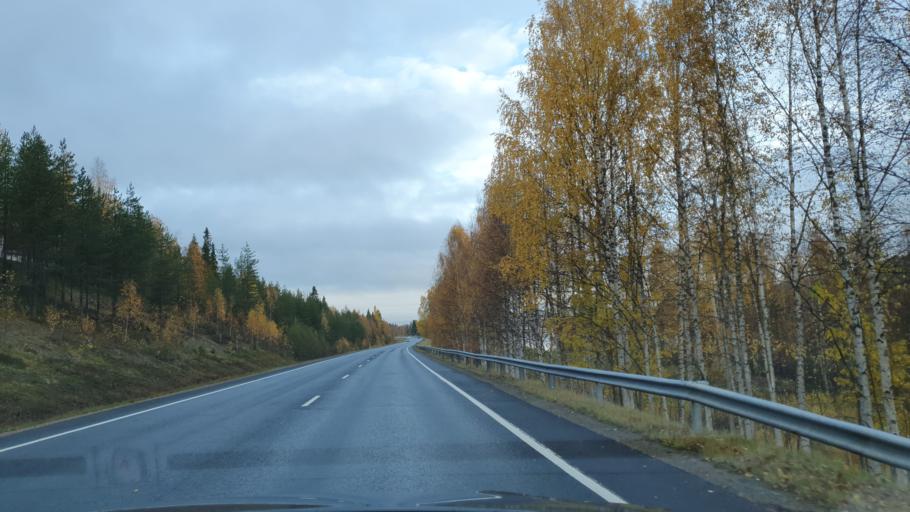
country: FI
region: Lapland
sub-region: Rovaniemi
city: Rovaniemi
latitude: 66.6059
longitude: 25.5763
